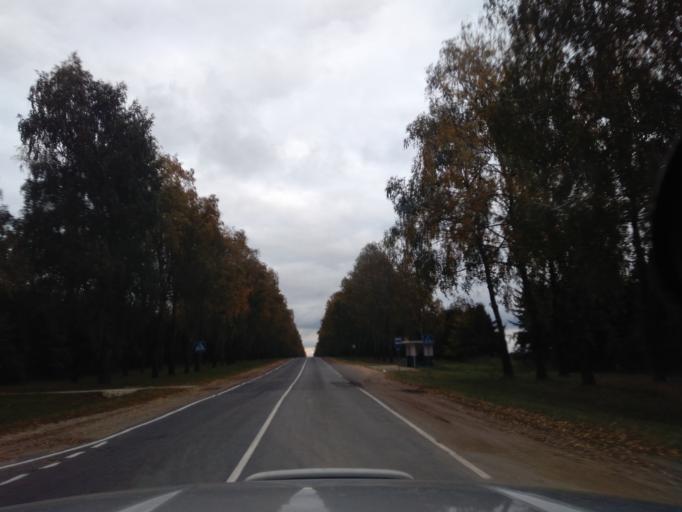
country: BY
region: Minsk
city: Slutsk
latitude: 53.2188
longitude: 27.4468
